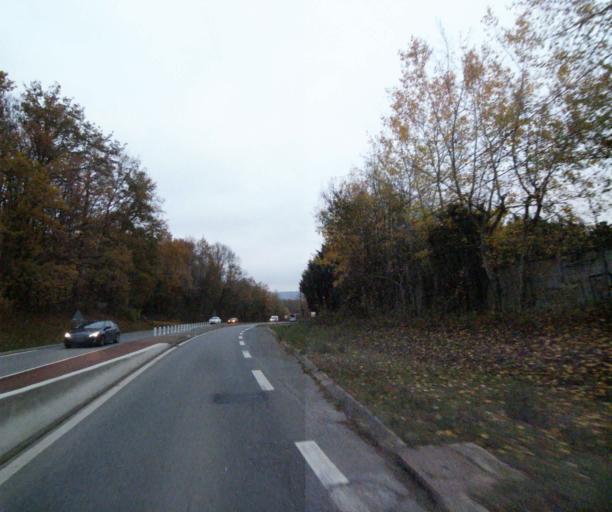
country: FR
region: Ile-de-France
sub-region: Departement des Yvelines
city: Villennes-sur-Seine
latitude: 48.9515
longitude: 1.9789
